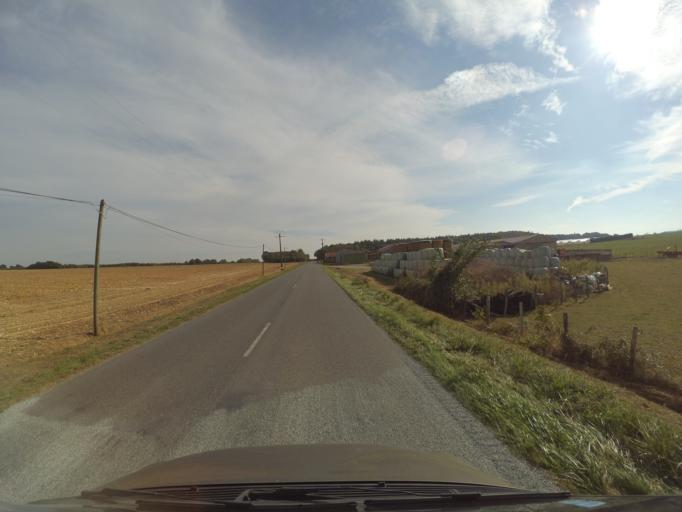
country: FR
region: Pays de la Loire
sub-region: Departement de Maine-et-Loire
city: Geste
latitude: 47.1827
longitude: -1.0770
